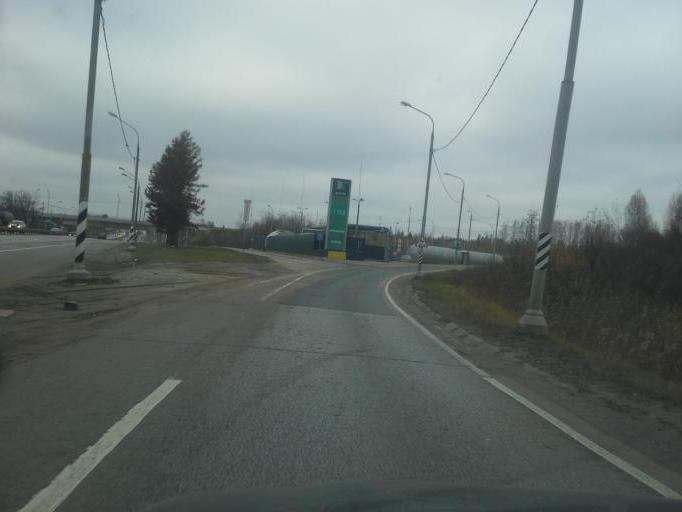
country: RU
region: Moskovskaya
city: Peshki
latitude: 56.1487
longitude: 37.0392
